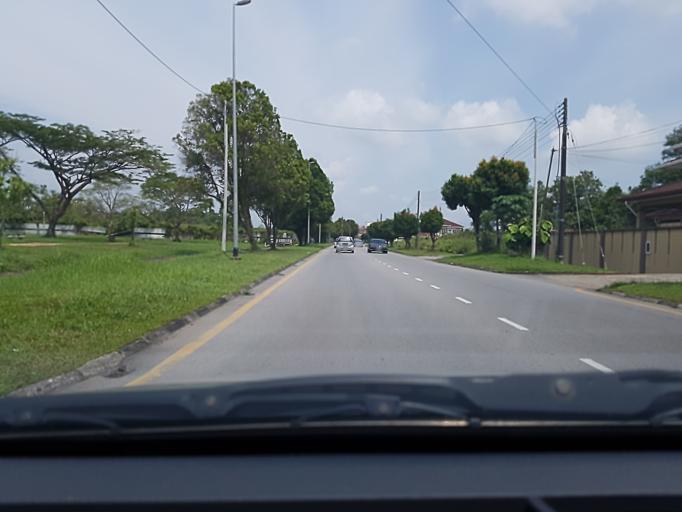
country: MY
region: Sarawak
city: Kuching
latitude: 1.5219
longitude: 110.3702
